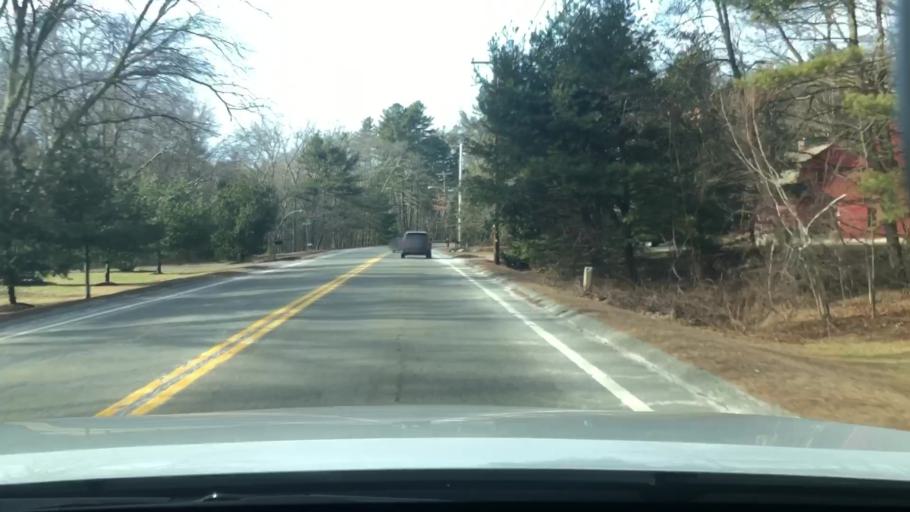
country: US
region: Massachusetts
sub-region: Worcester County
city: Northbridge
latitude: 42.1766
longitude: -71.6362
